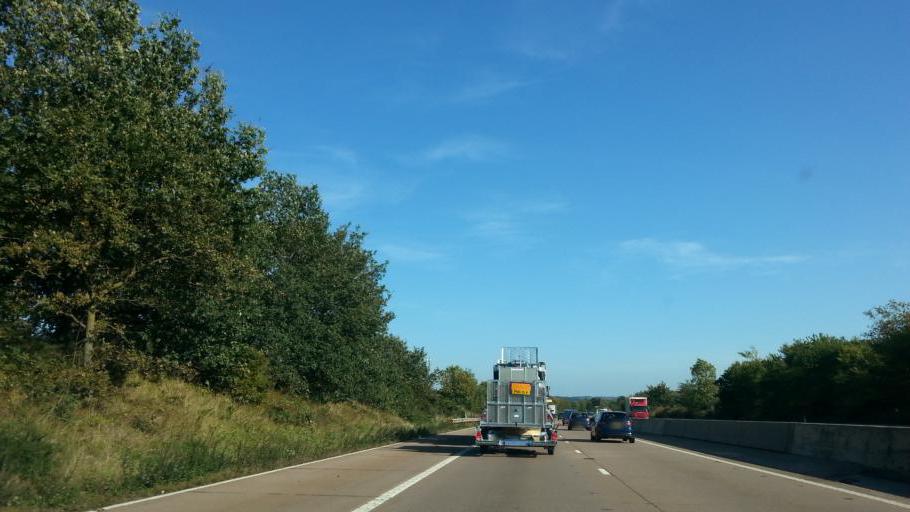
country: GB
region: England
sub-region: Shropshire
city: Shifnal
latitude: 52.6752
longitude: -2.3499
